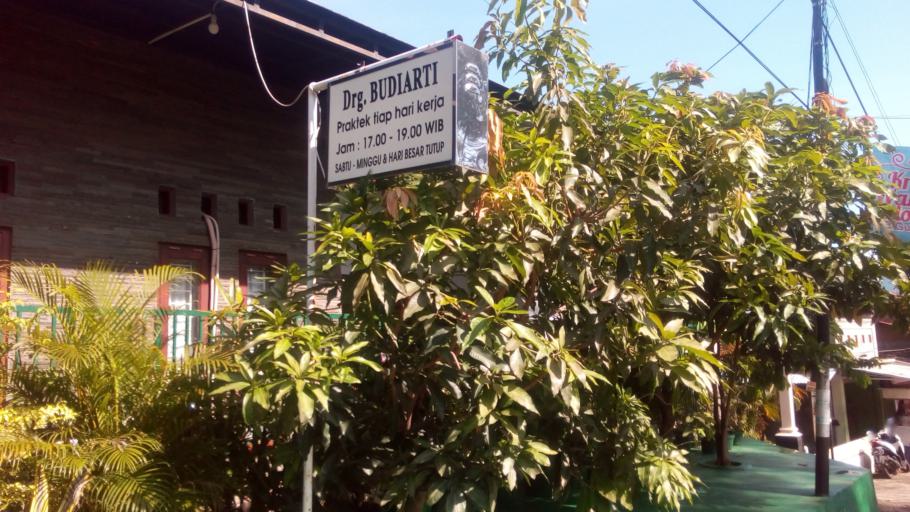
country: ID
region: Central Java
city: Ungaran
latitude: -7.0695
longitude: 110.4202
